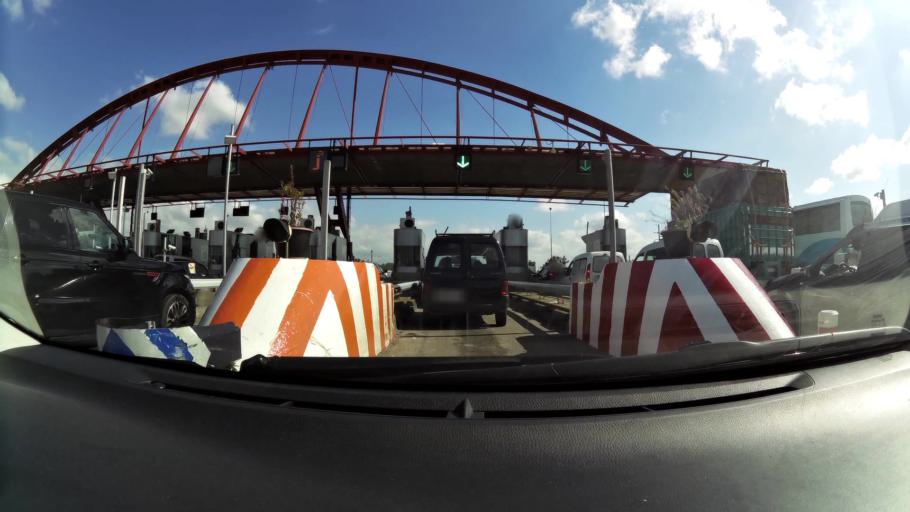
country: MA
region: Chaouia-Ouardigha
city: Nouaseur
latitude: 33.3689
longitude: -7.6208
